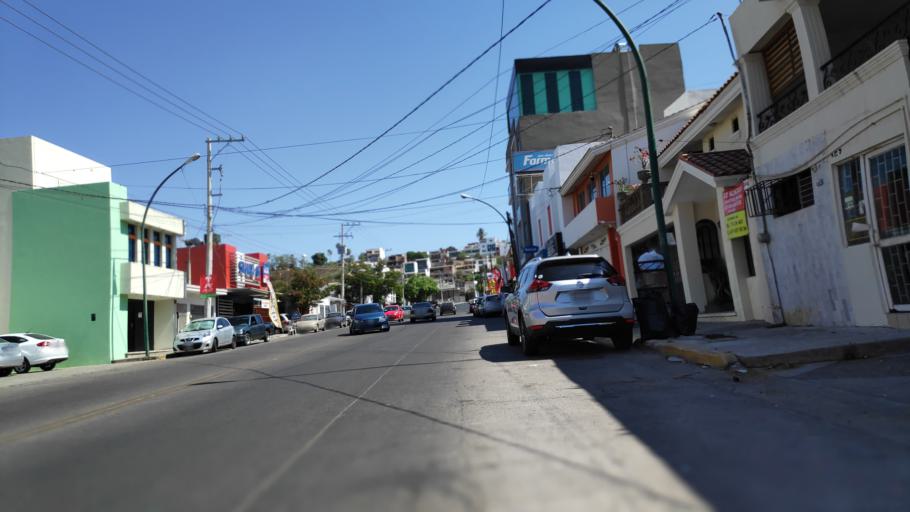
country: MX
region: Sinaloa
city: Culiacan
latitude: 24.7875
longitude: -107.4005
